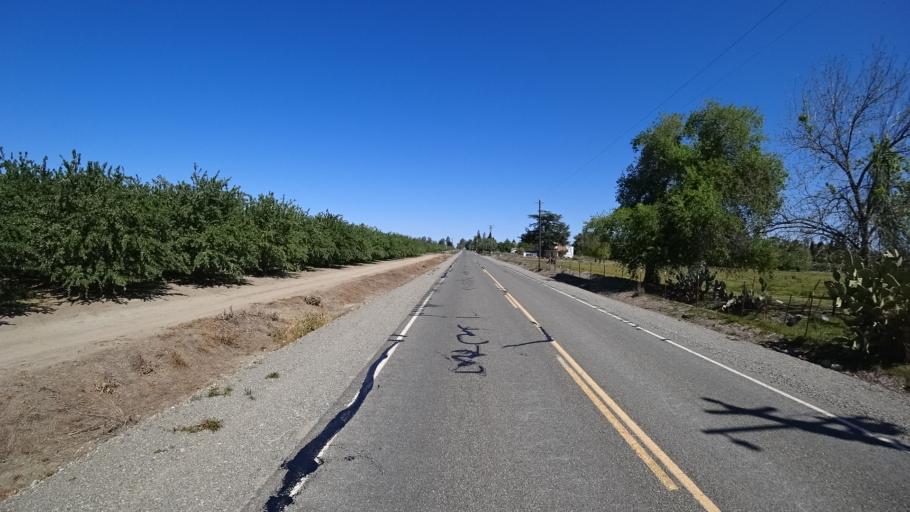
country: US
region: California
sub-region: Glenn County
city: Orland
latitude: 39.7421
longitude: -122.1410
